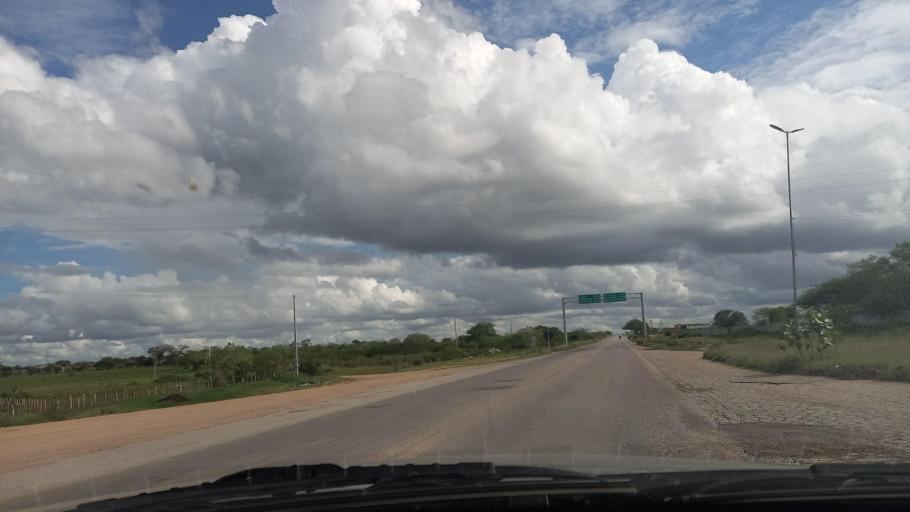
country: BR
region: Pernambuco
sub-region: Cachoeirinha
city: Cachoeirinha
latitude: -8.4941
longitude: -36.2378
